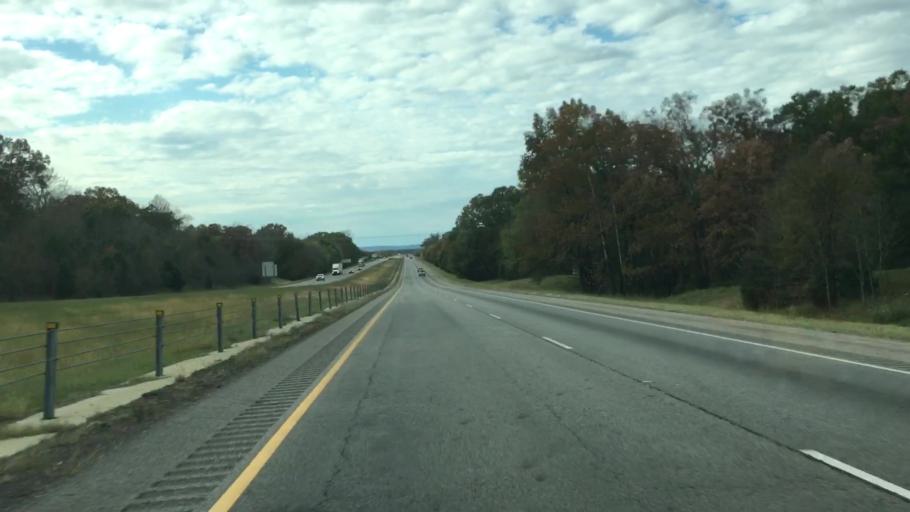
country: US
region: Arkansas
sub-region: Conway County
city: Morrilton
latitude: 35.1818
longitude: -92.7625
